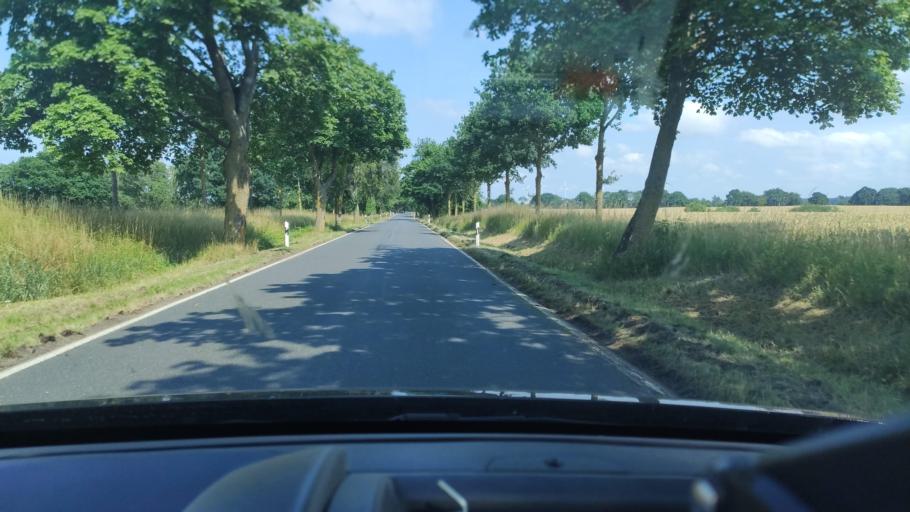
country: DE
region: Mecklenburg-Vorpommern
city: Grimmen
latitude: 54.0502
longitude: 13.0763
